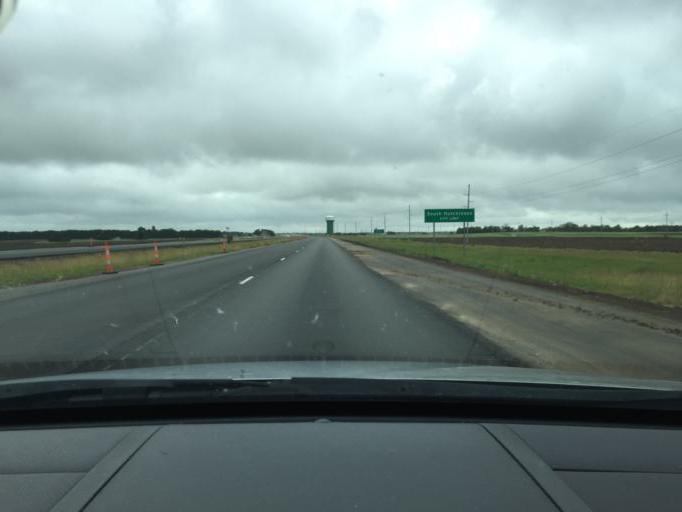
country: US
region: Kansas
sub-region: Reno County
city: South Hutchinson
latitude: 38.0133
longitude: -97.9587
